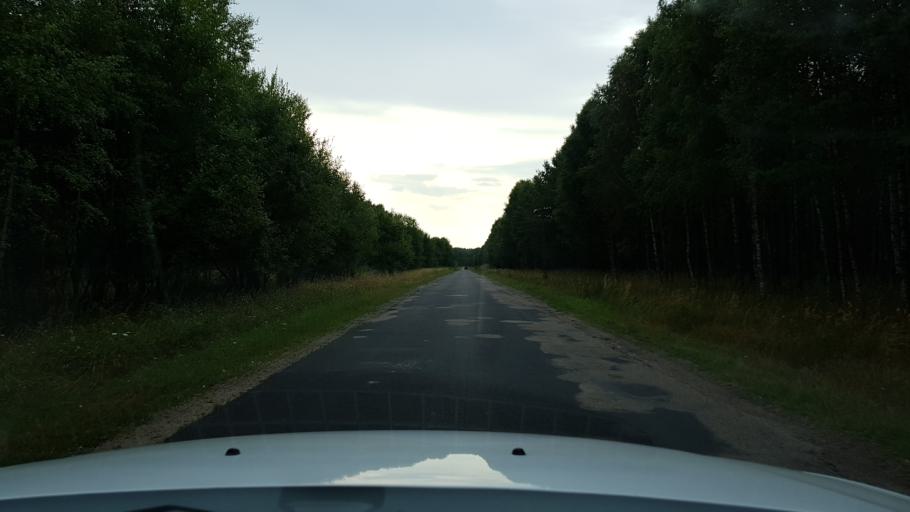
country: PL
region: West Pomeranian Voivodeship
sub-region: Powiat drawski
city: Wierzchowo
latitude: 53.4461
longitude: 16.1523
